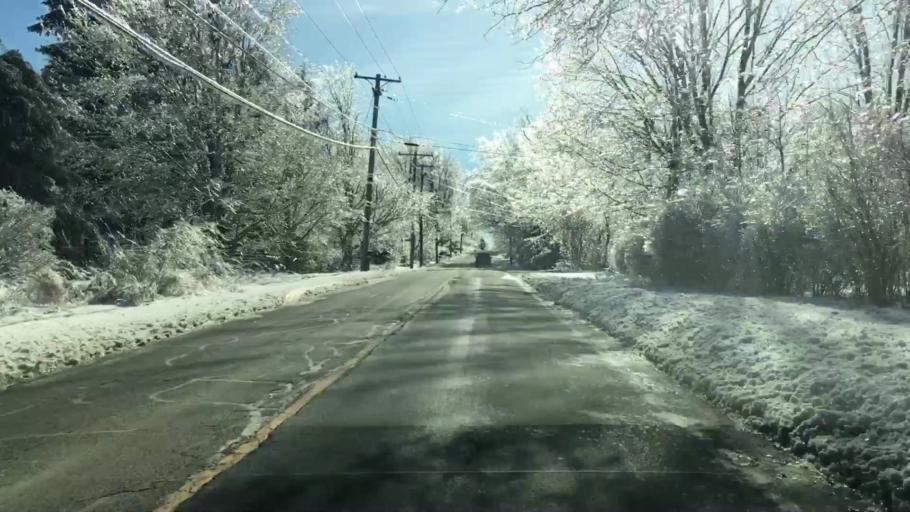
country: US
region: Connecticut
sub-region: Fairfield County
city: Newtown
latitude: 41.3919
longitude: -73.2587
